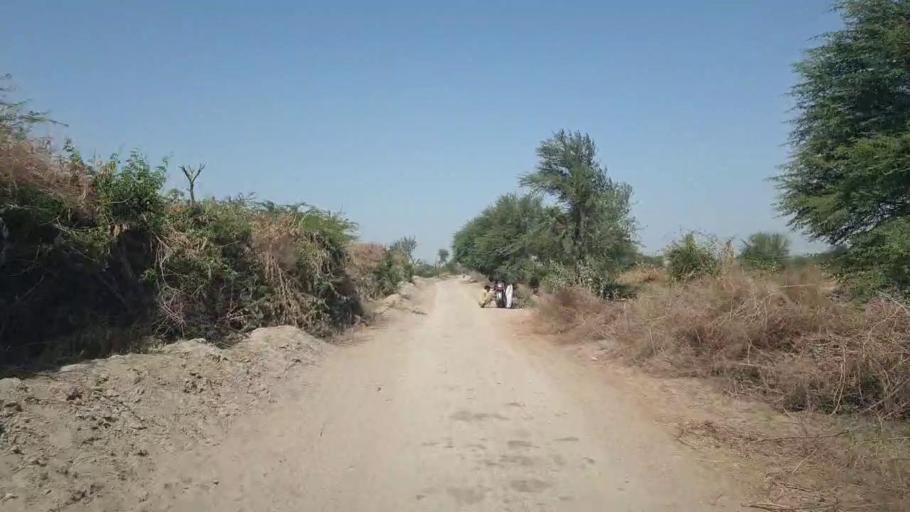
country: PK
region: Sindh
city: Kunri
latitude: 25.2793
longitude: 69.6294
